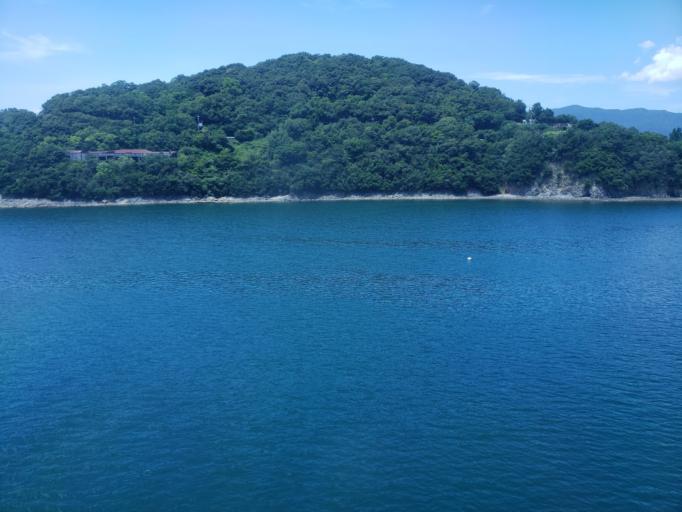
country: JP
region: Kagawa
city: Tonosho
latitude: 34.4546
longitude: 134.3173
